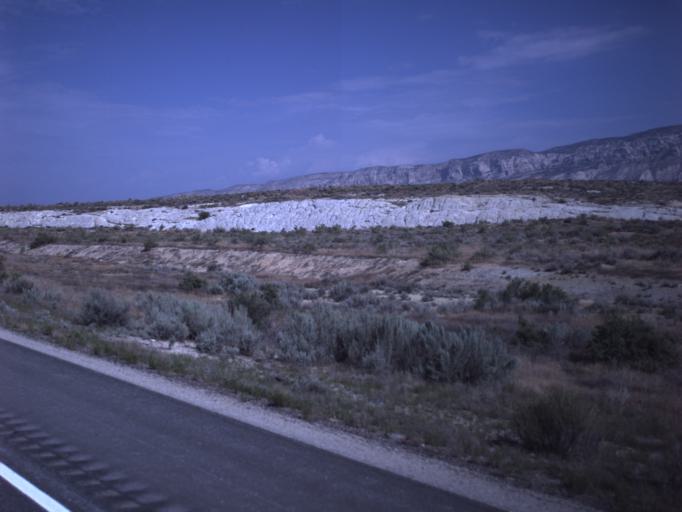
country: US
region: Colorado
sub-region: Rio Blanco County
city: Rangely
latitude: 40.2864
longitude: -109.1335
